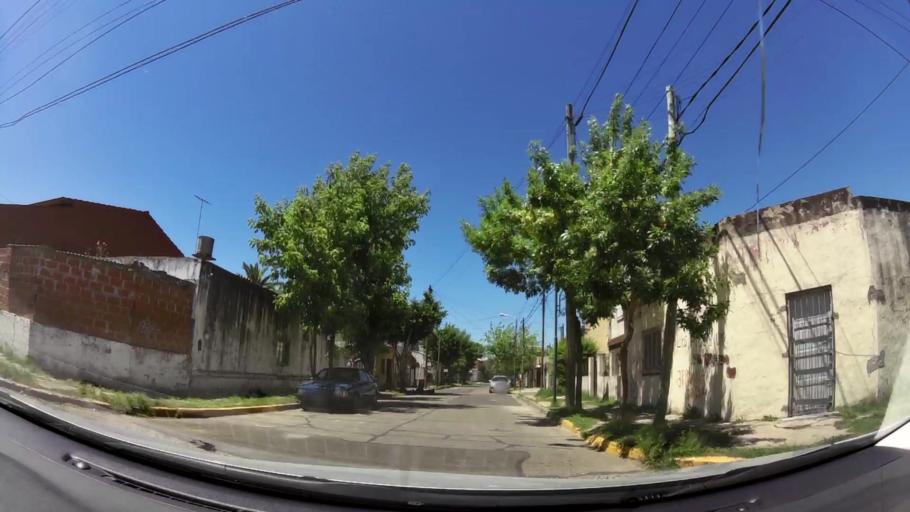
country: AR
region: Buenos Aires
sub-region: Partido de Tigre
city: Tigre
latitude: -34.4493
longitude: -58.5556
